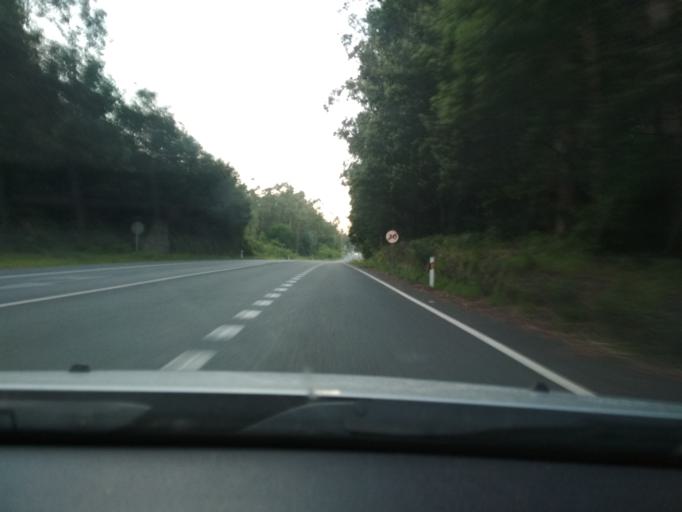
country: ES
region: Galicia
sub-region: Provincia de Pontevedra
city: Caldas de Reis
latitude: 42.6301
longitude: -8.6489
